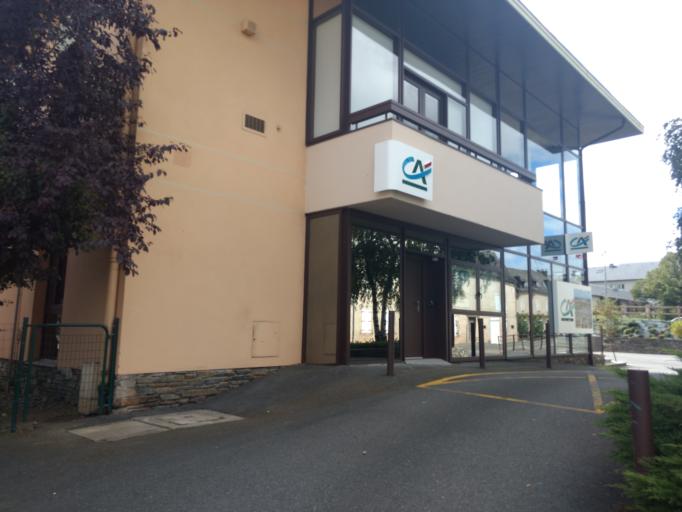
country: FR
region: Midi-Pyrenees
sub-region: Departement de l'Aveyron
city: Colombies
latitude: 44.4097
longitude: 2.2930
